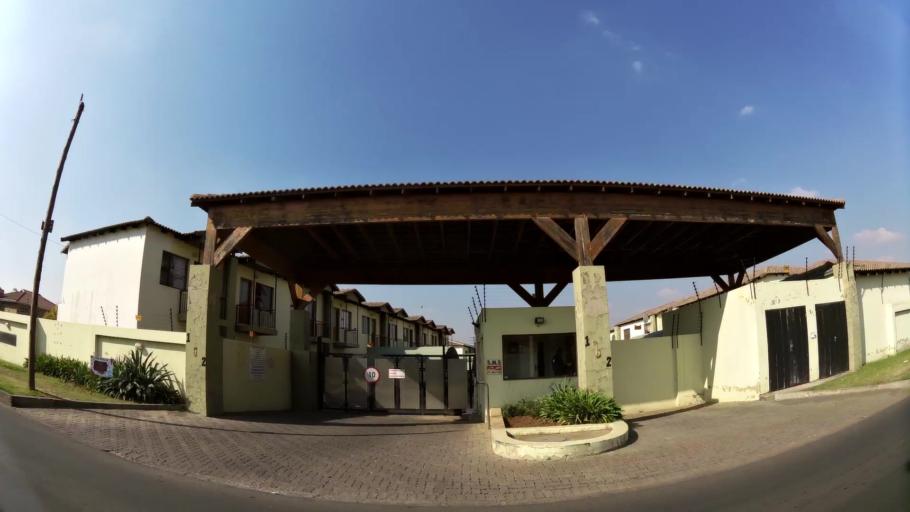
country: ZA
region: Gauteng
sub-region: Ekurhuleni Metropolitan Municipality
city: Boksburg
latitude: -26.1927
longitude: 28.2583
